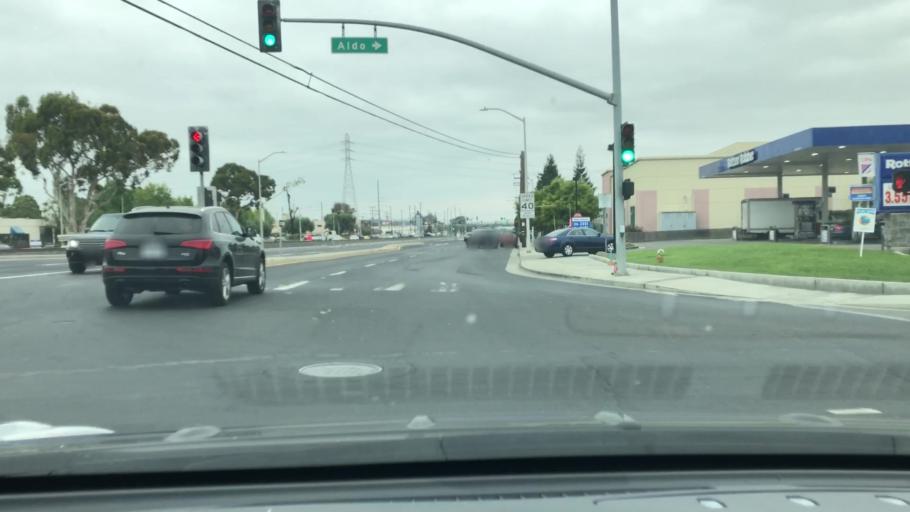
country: US
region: California
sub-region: Santa Clara County
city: Santa Clara
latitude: 37.3831
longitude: -121.9505
